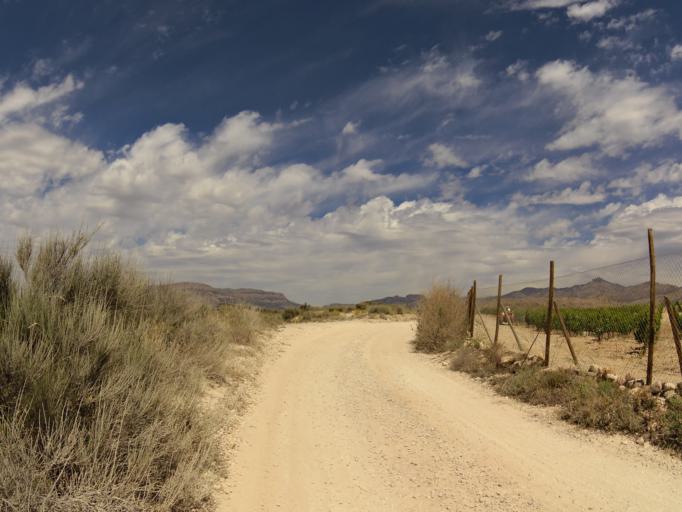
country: ES
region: Valencia
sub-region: Provincia de Alicante
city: Agost
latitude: 38.4022
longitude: -0.6097
